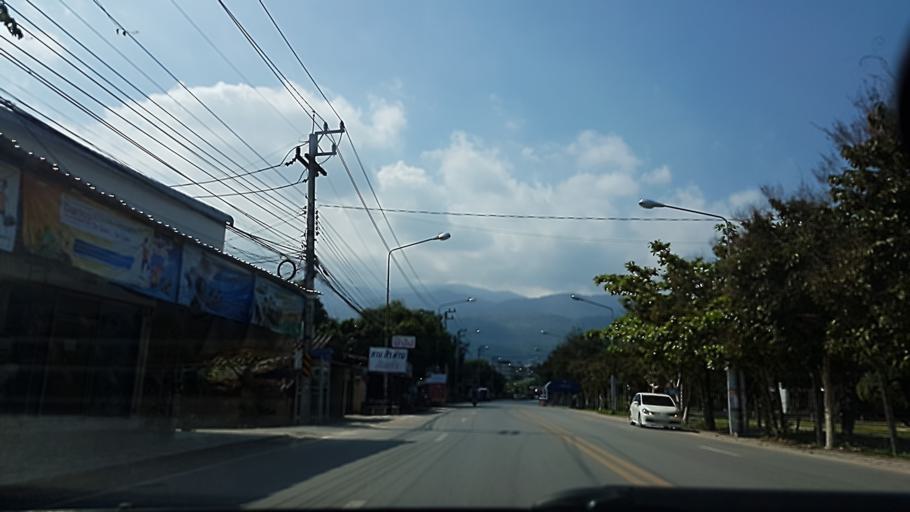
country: TH
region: Chiang Mai
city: Chiang Mai
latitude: 18.8218
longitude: 98.9690
